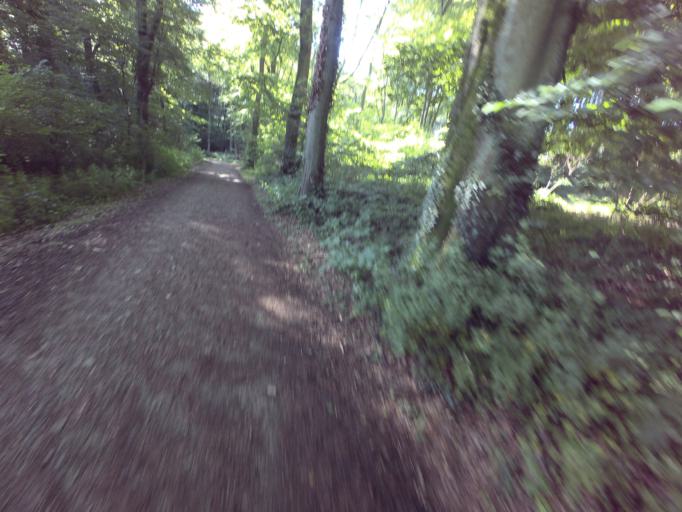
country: NL
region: Limburg
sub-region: Gemeente Vaals
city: Vaals
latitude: 50.7583
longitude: 6.0230
